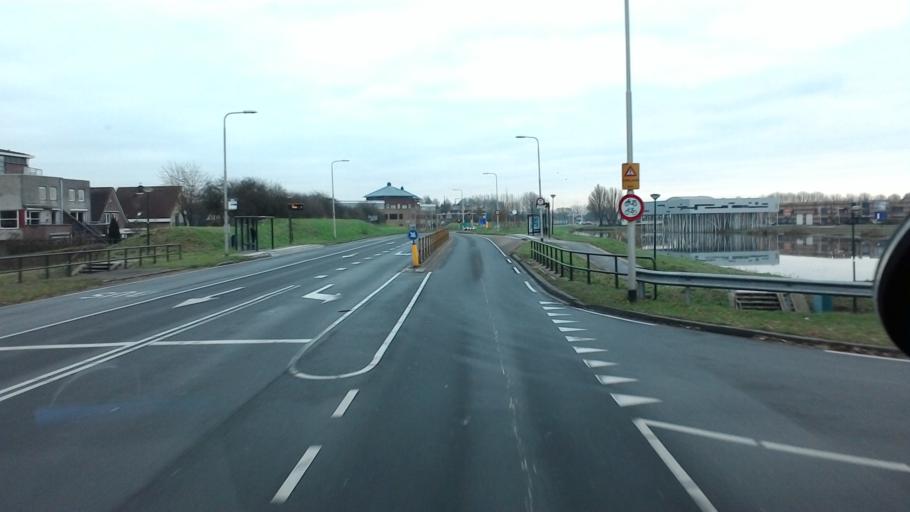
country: NL
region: Utrecht
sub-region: Gemeente Houten
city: Houten
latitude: 52.0294
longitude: 5.1441
